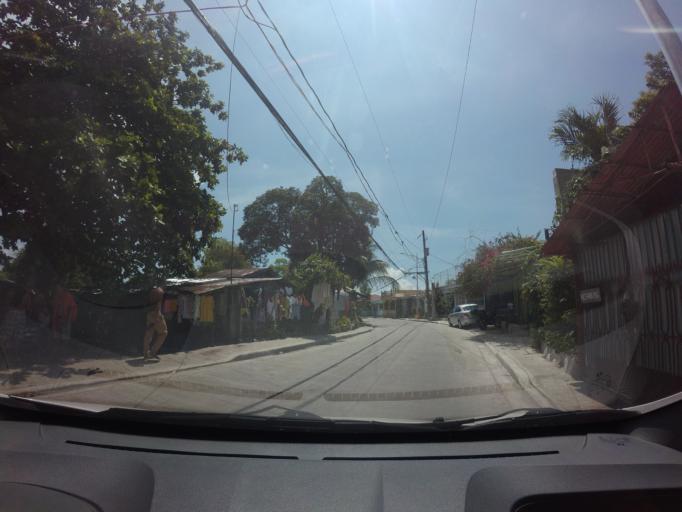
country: PH
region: Calabarzon
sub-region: Province of Rizal
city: Las Pinas
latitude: 14.4228
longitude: 120.9894
